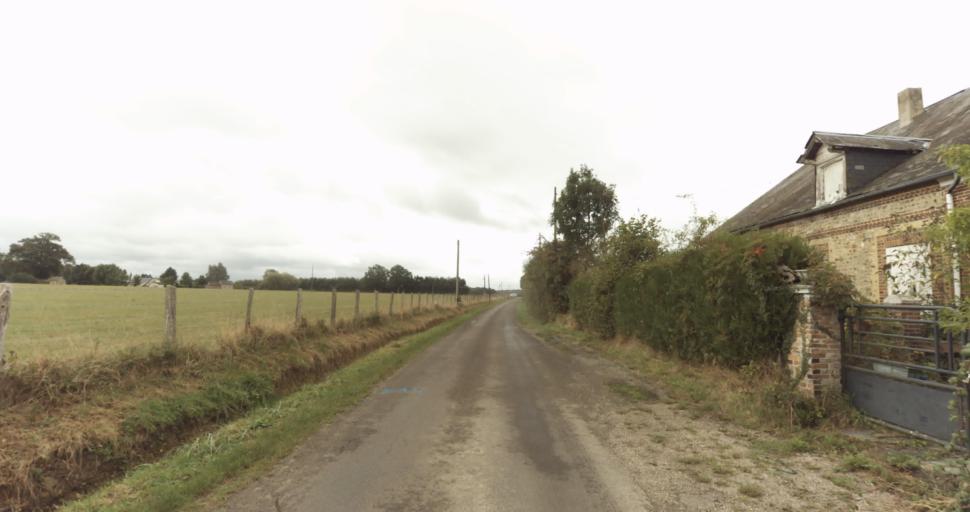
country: FR
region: Lower Normandy
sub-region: Departement de l'Orne
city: Sainte-Gauburge-Sainte-Colombe
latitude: 48.7188
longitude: 0.4891
